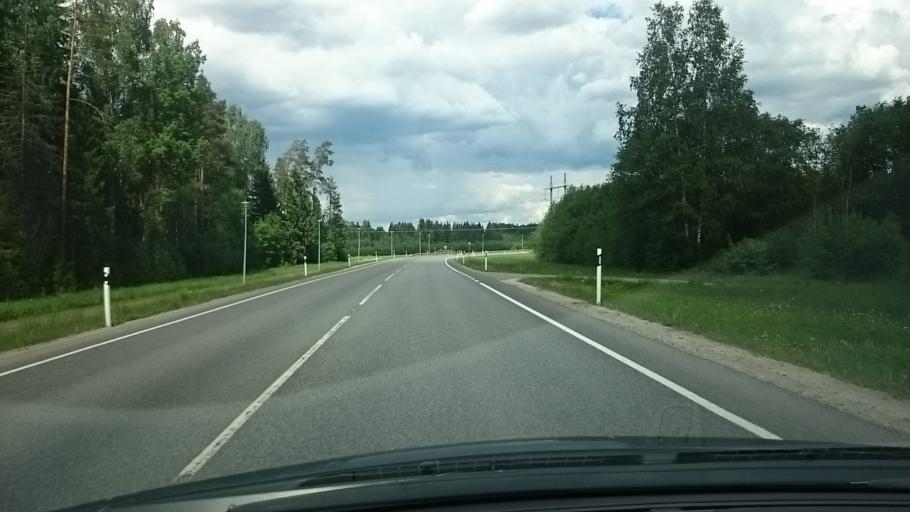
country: EE
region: Jaervamaa
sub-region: Paide linn
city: Paide
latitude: 58.8704
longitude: 25.4948
